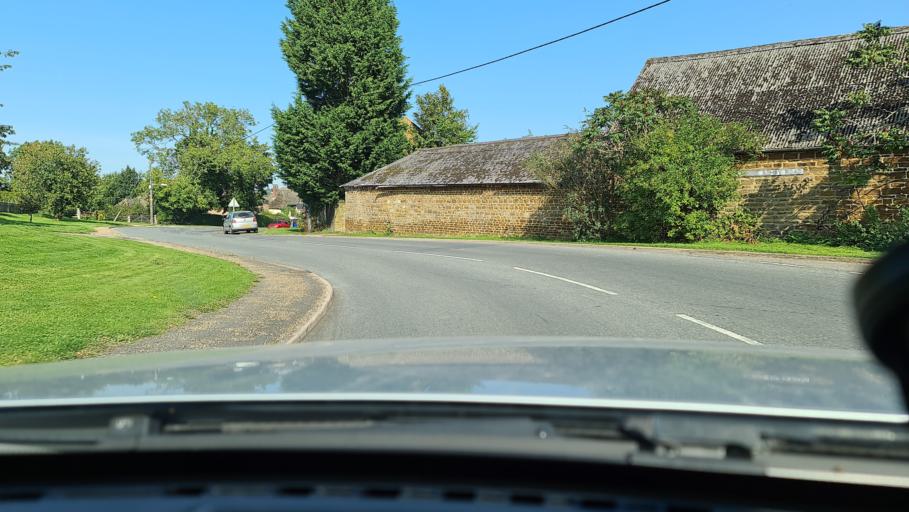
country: GB
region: England
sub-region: Northamptonshire
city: Brackley
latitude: 52.1394
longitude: -1.1588
